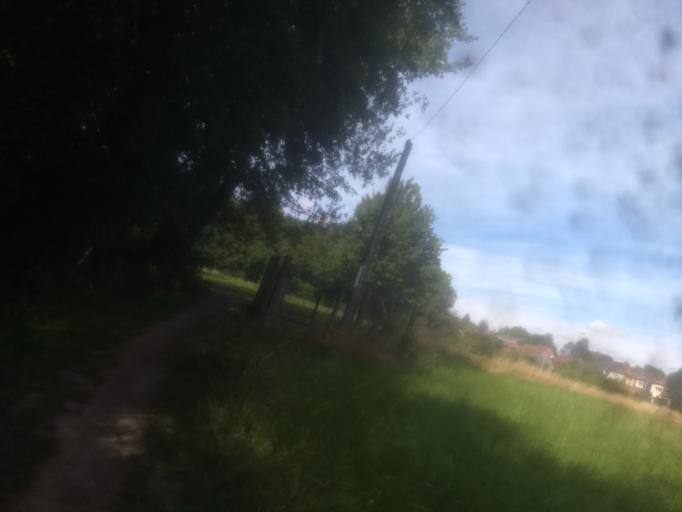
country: FR
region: Nord-Pas-de-Calais
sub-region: Departement du Pas-de-Calais
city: Agny
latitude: 50.2659
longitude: 2.7584
